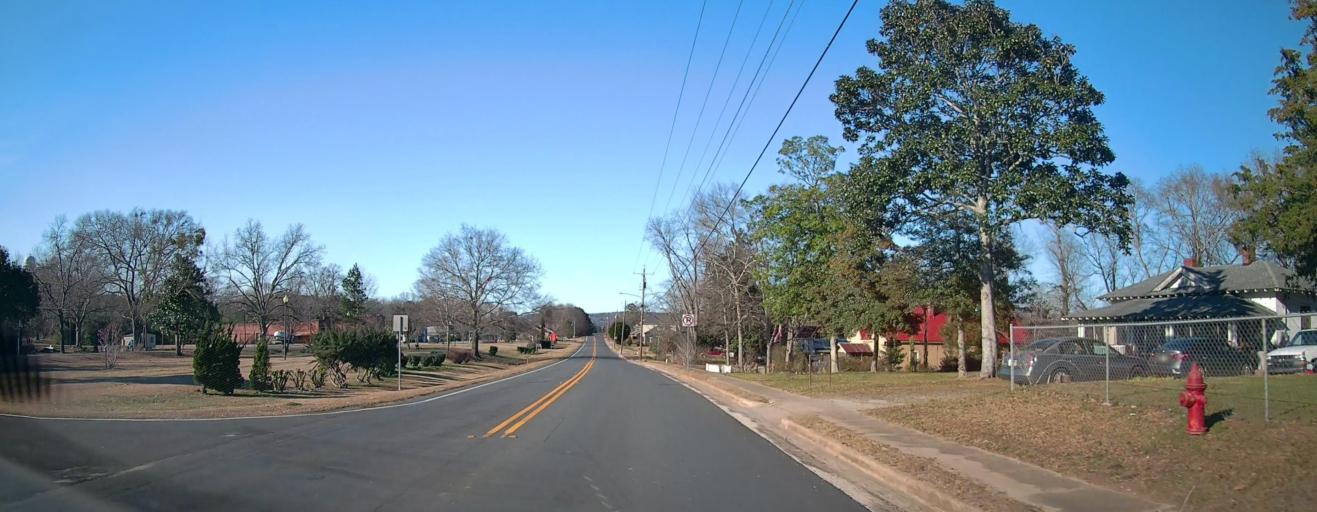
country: US
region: Georgia
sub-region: Talbot County
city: Sardis
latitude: 32.8075
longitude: -84.6960
